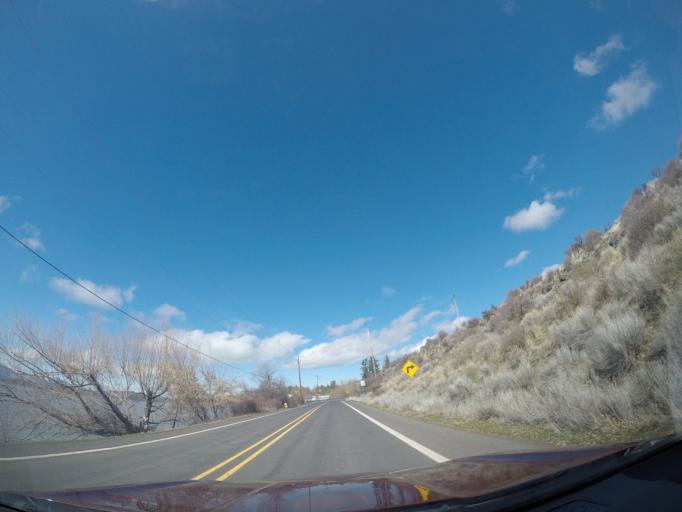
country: US
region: Oregon
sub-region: Klamath County
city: Klamath Falls
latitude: 42.2363
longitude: -121.8081
